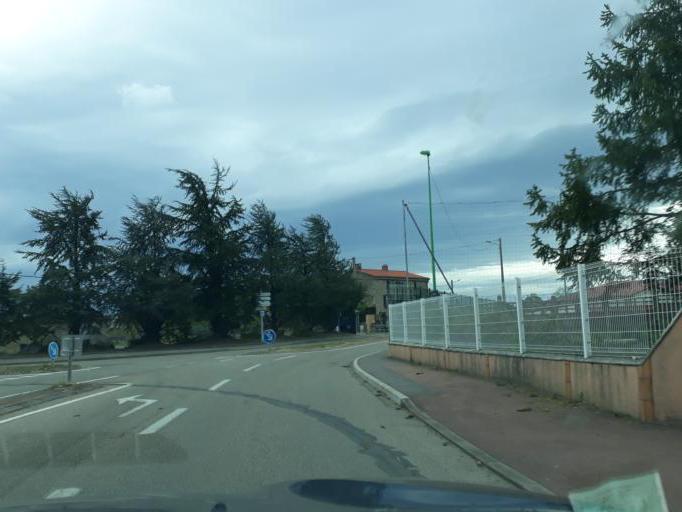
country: FR
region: Rhone-Alpes
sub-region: Departement du Rhone
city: Soucieu-en-Jarrest
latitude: 45.6775
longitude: 4.6934
